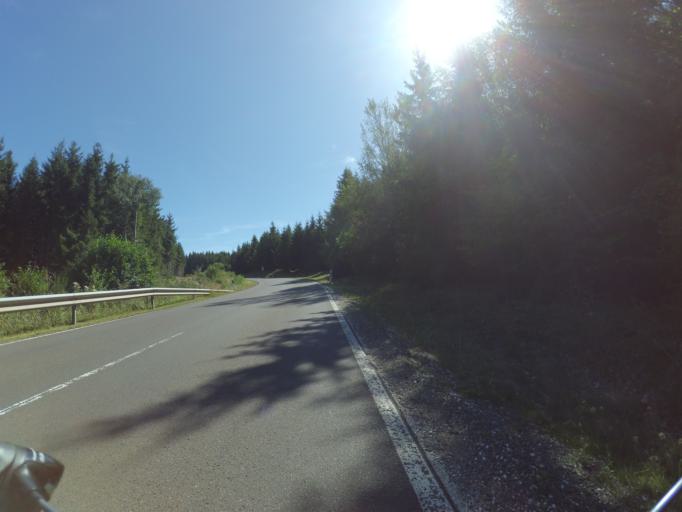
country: DE
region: Rheinland-Pfalz
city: Deuselbach
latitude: 49.7431
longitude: 7.0702
